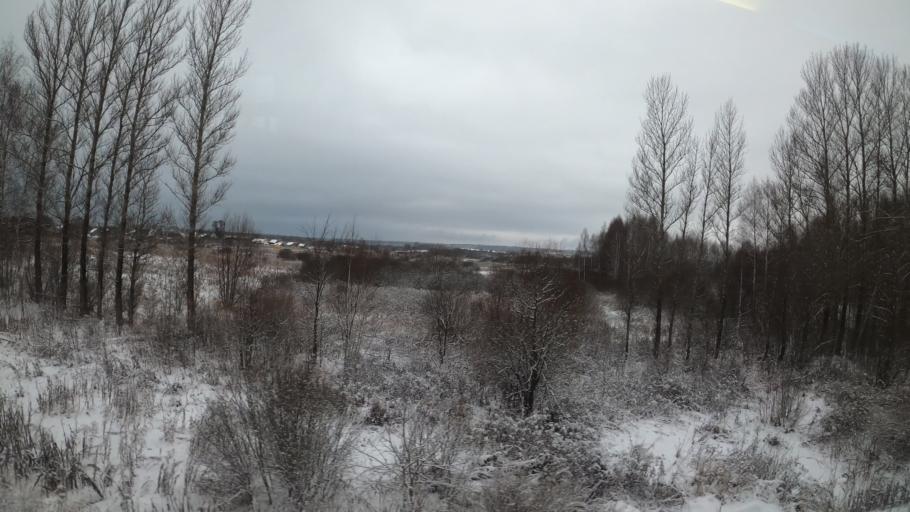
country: RU
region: Jaroslavl
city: Pereslavl'-Zalesskiy
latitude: 56.6883
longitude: 38.9179
